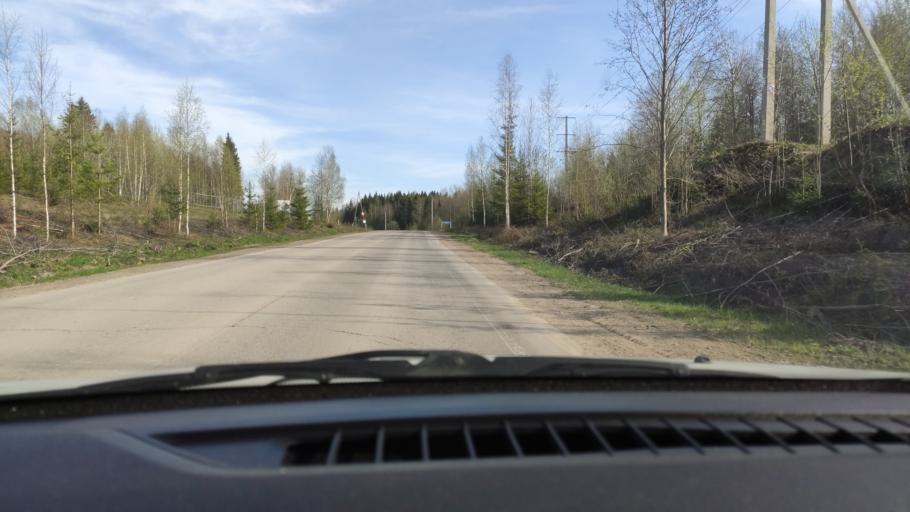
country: RU
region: Perm
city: Novyye Lyady
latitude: 57.9266
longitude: 56.6514
